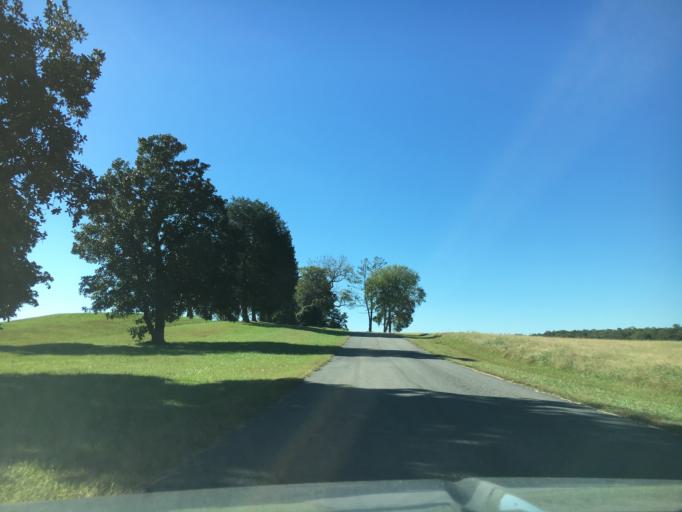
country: US
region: Virginia
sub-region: Goochland County
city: Goochland
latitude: 37.6979
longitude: -77.8324
